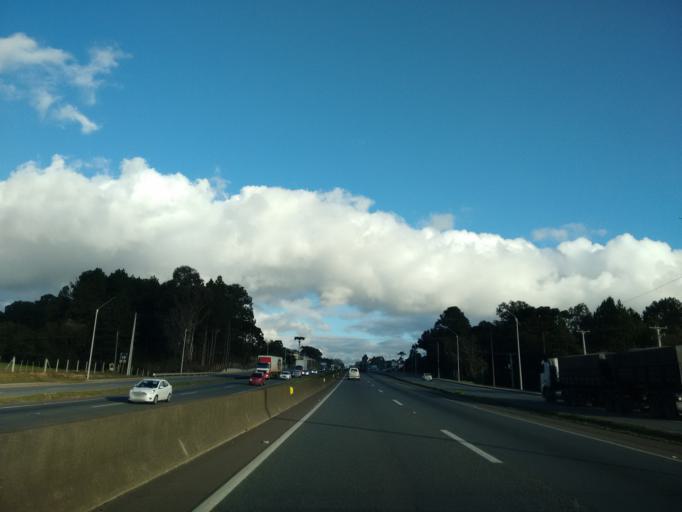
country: BR
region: Parana
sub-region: Sao Jose Dos Pinhais
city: Sao Jose dos Pinhais
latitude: -25.7033
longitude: -49.1422
